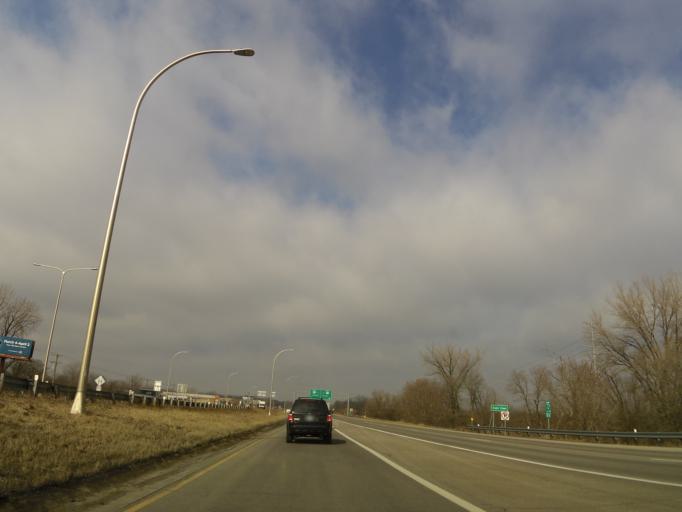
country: US
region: Minnesota
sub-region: Scott County
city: Savage
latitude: 44.7806
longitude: -93.3817
